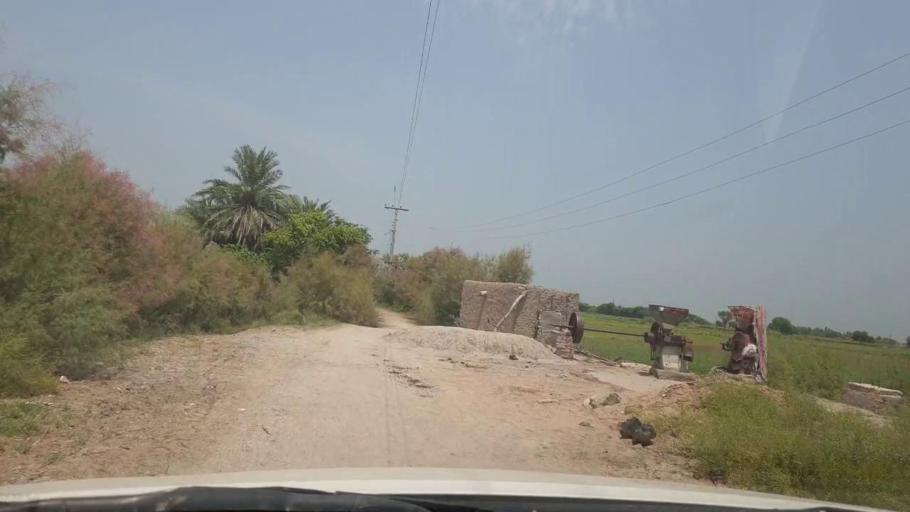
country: PK
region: Sindh
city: Rustam jo Goth
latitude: 28.0588
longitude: 68.7533
